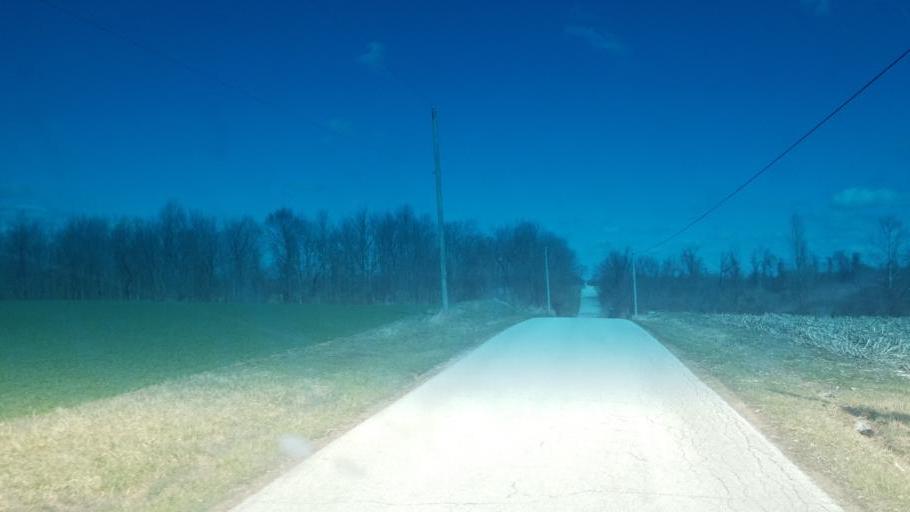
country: US
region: Ohio
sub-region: Crawford County
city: Bucyrus
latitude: 40.8428
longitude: -83.0739
